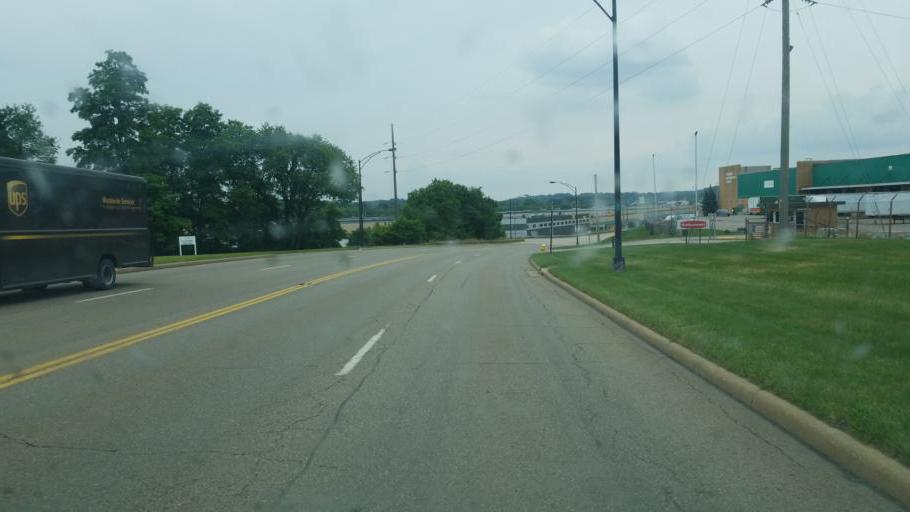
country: US
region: Ohio
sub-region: Summit County
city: Mogadore
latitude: 41.0590
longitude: -81.4200
